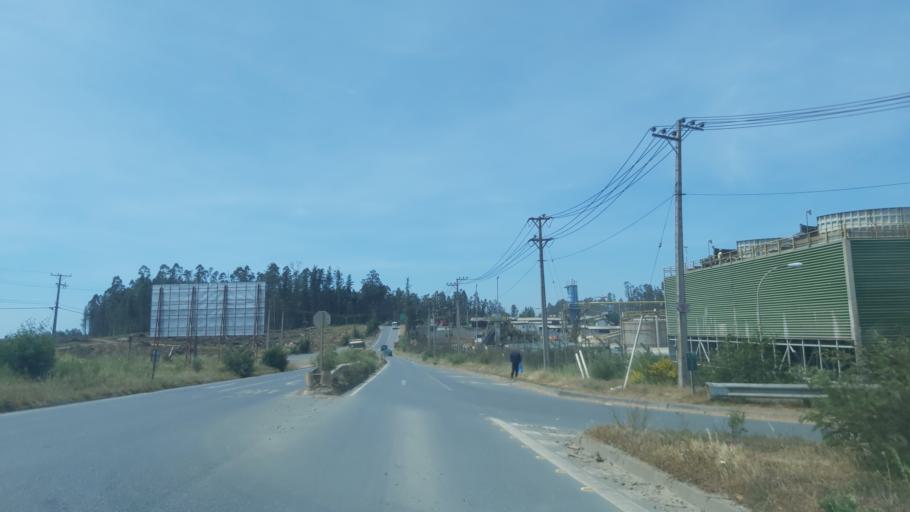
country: CL
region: Maule
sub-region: Provincia de Talca
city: Constitucion
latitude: -35.3706
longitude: -72.4121
